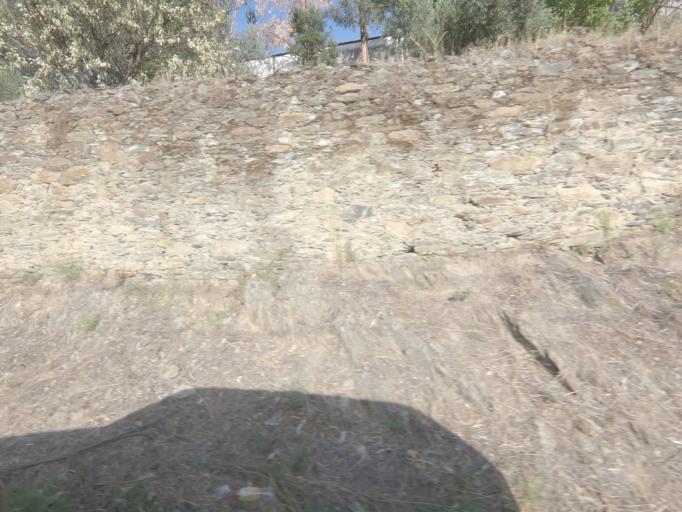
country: PT
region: Vila Real
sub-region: Sabrosa
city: Vilela
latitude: 41.2093
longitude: -7.5409
